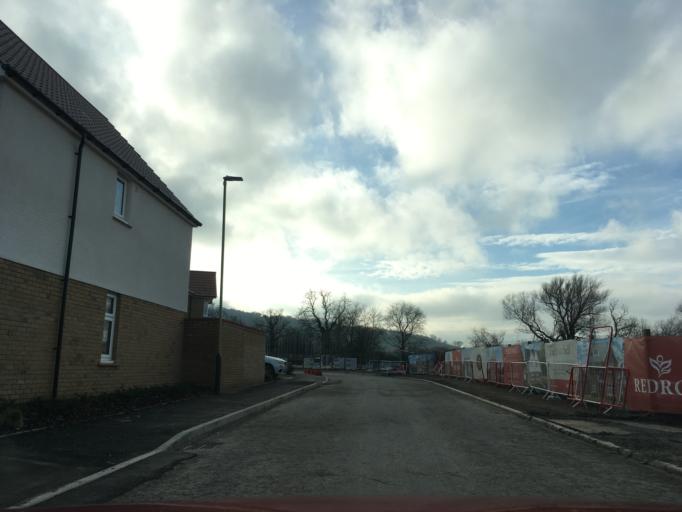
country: GB
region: England
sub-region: Gloucestershire
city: Shurdington
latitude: 51.8732
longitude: -2.0960
